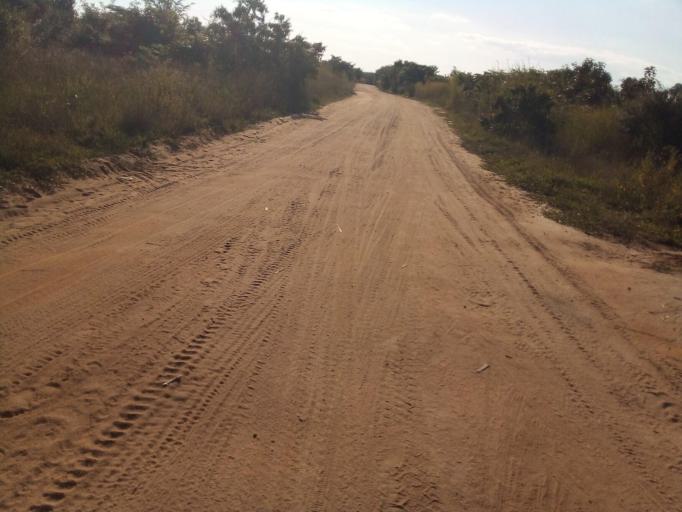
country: MZ
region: Zambezia
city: Quelimane
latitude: -17.5104
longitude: 36.8329
